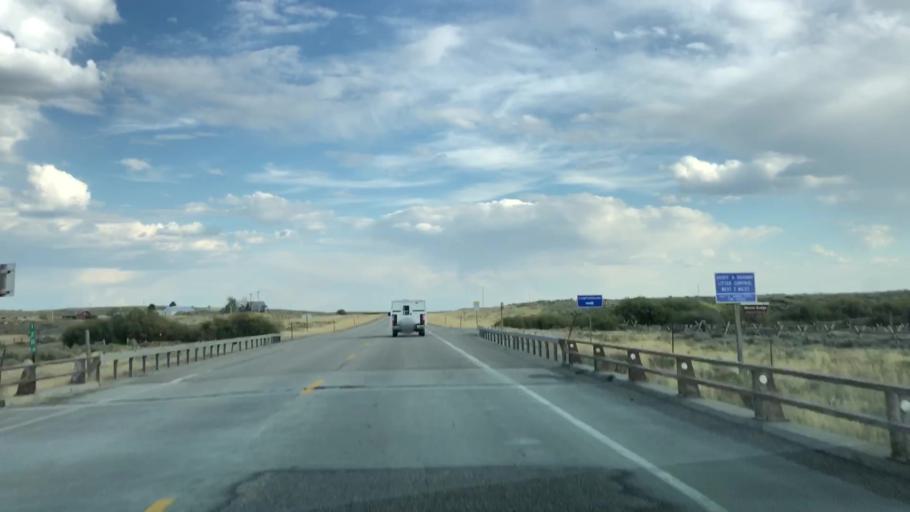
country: US
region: Wyoming
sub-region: Sublette County
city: Pinedale
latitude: 43.0186
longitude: -110.1187
